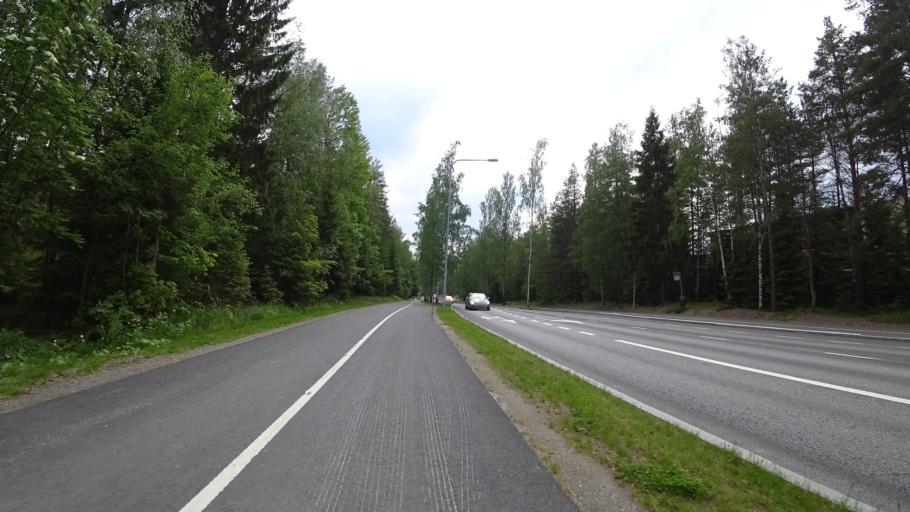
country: FI
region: Pirkanmaa
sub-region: Tampere
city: Pirkkala
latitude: 61.5042
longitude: 23.6049
